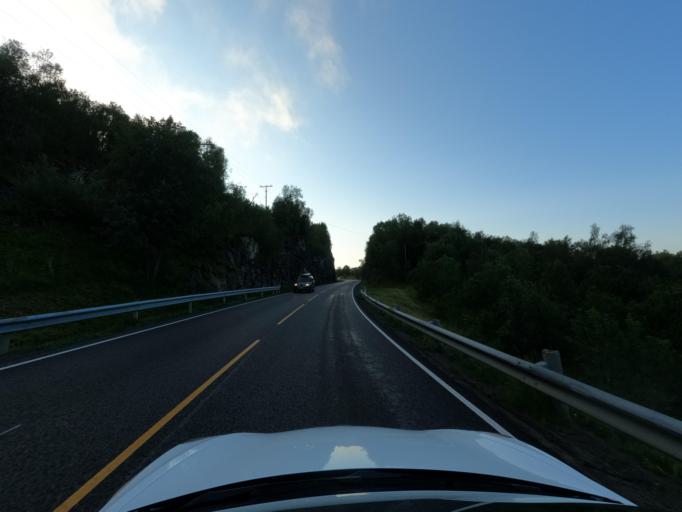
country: NO
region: Troms
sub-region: Skanland
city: Evenskjer
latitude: 68.6720
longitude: 16.5703
